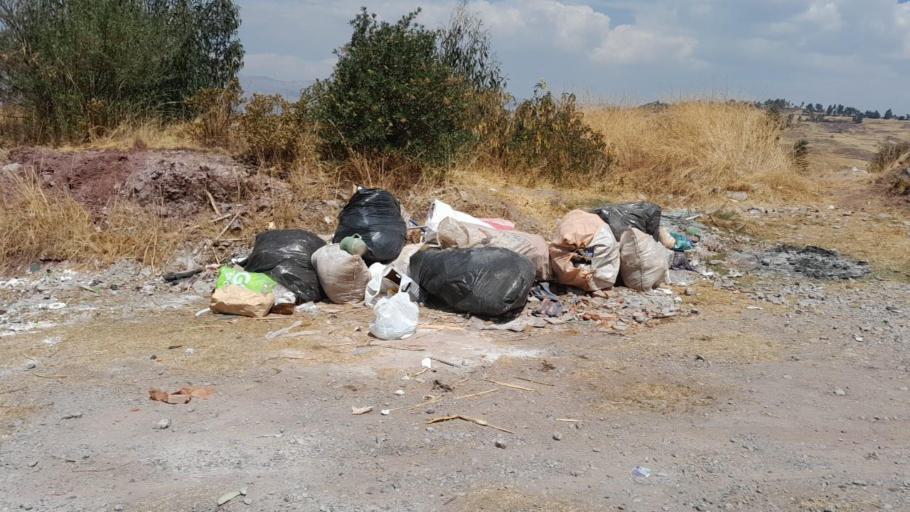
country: PE
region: Cusco
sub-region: Provincia de Cusco
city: Cusco
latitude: -13.4958
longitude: -71.9301
